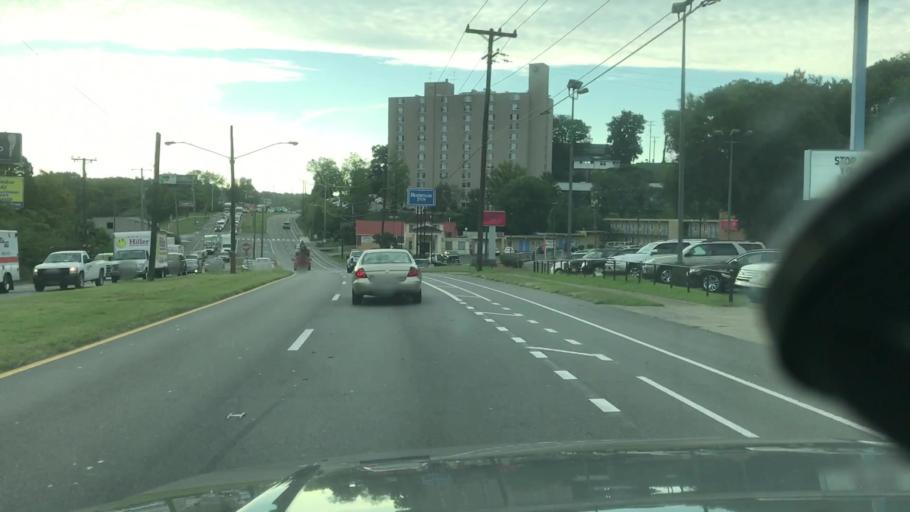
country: US
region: Tennessee
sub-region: Davidson County
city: Nashville
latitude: 36.1333
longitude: -86.7217
